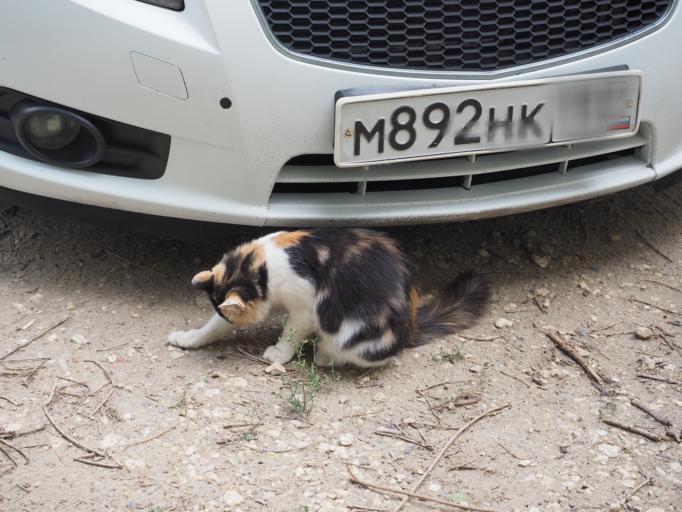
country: RU
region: Volgograd
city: Volgograd
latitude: 48.6938
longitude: 44.5015
